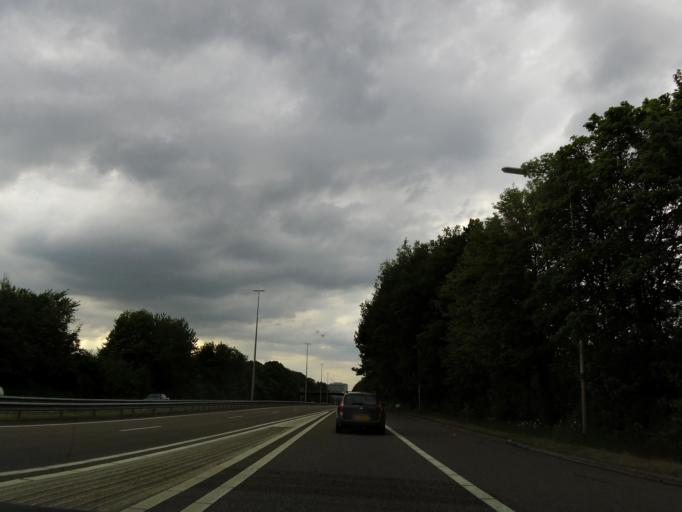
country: NL
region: Limburg
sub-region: Gemeente Heerlen
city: Heerlen
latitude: 50.8599
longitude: 5.9963
